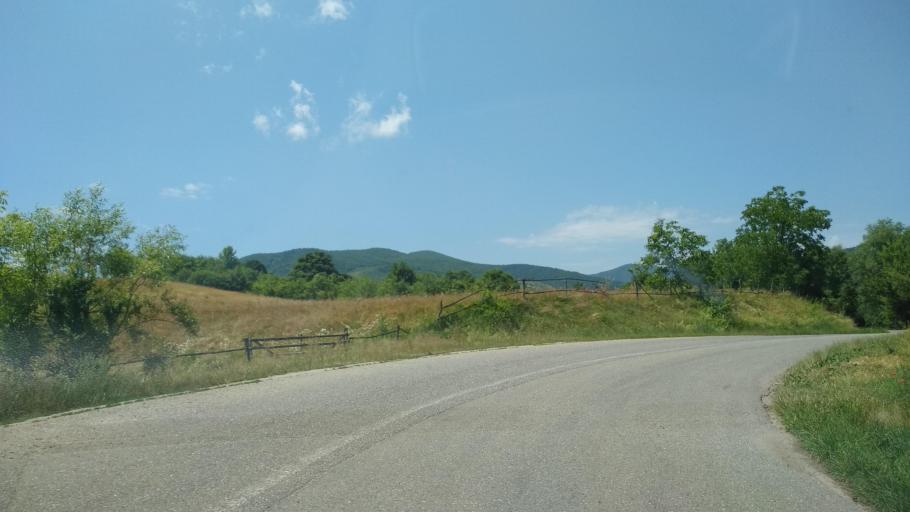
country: RO
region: Hunedoara
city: Densus
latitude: 45.5792
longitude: 22.8178
